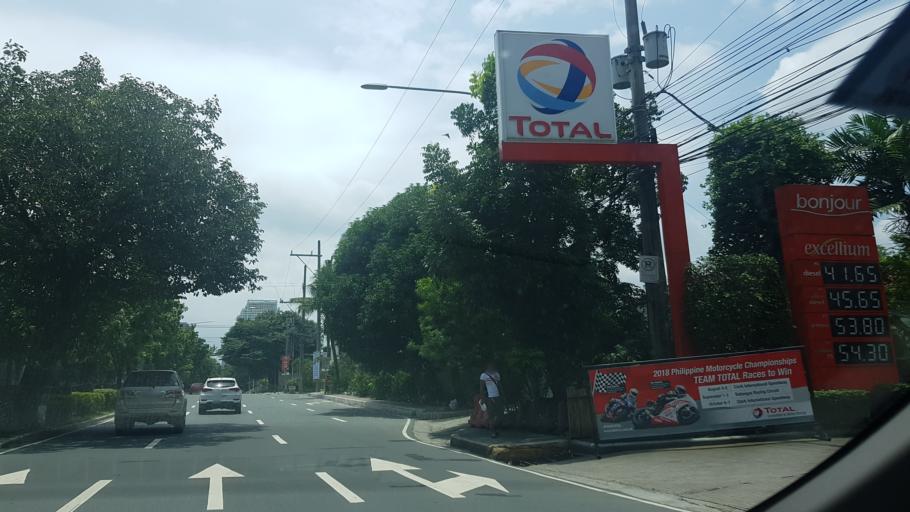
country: PH
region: Metro Manila
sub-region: San Juan
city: San Juan
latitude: 14.6069
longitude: 121.0400
